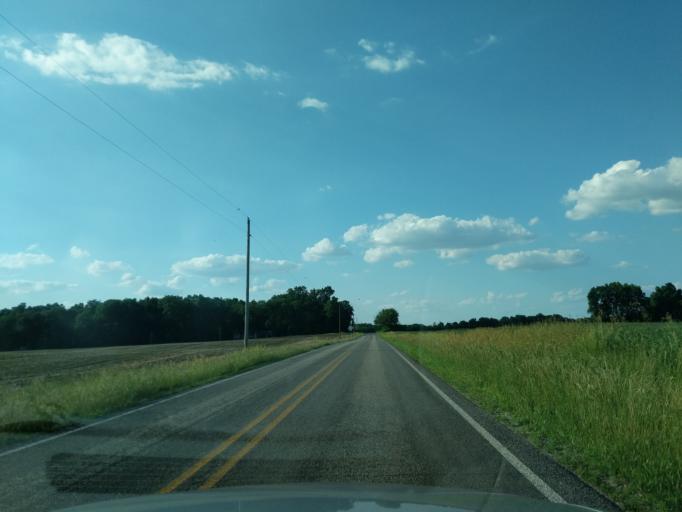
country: US
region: Indiana
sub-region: Kosciusko County
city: North Webster
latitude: 41.2993
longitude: -85.6431
